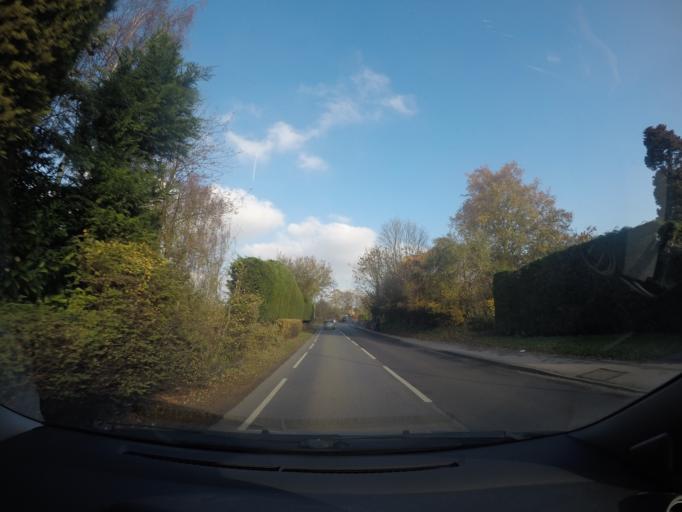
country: GB
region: England
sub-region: City of York
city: Huntington
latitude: 53.9934
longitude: -1.0620
